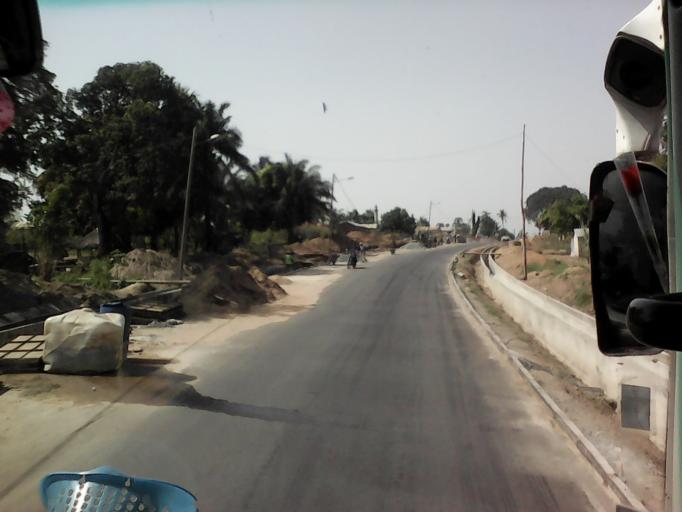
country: TG
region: Centrale
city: Sotouboua
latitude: 8.6773
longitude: 1.0248
